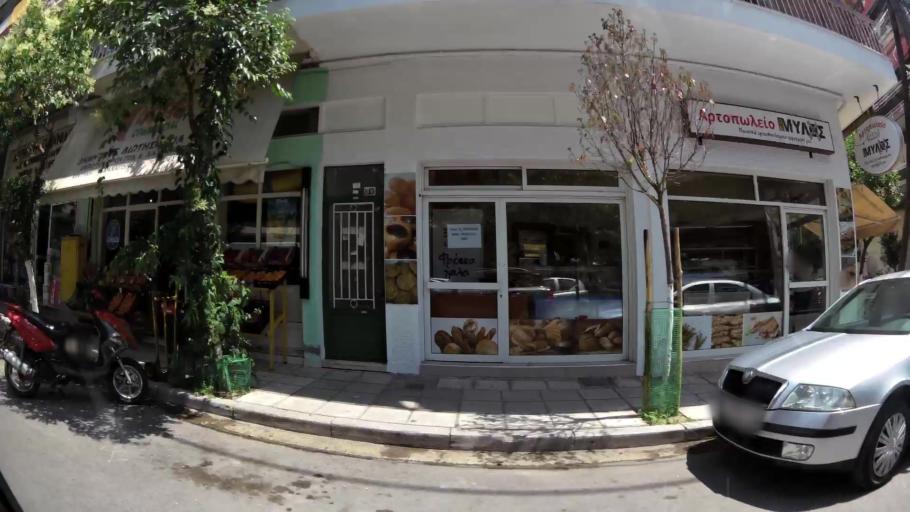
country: GR
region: Central Macedonia
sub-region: Nomos Thessalonikis
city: Ampelokipoi
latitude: 40.6546
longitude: 22.9307
